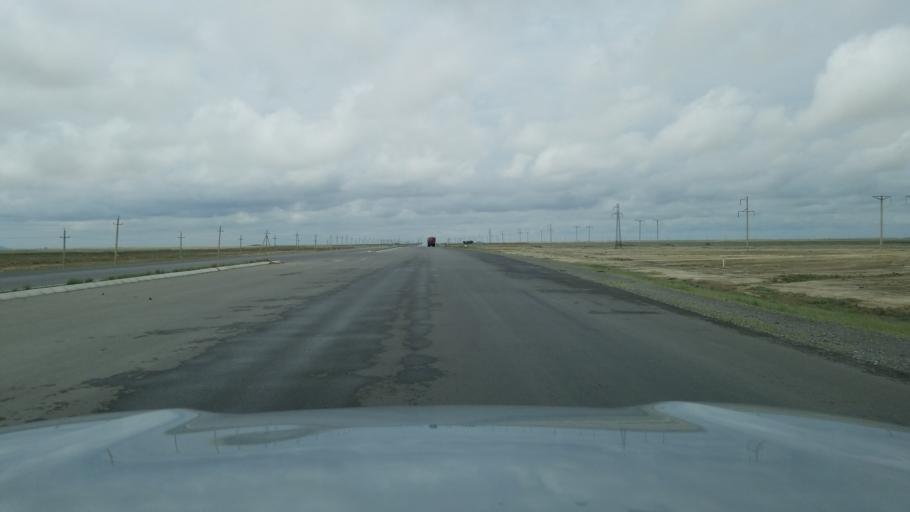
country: TM
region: Balkan
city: Gazanjyk
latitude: 39.2088
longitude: 55.7556
